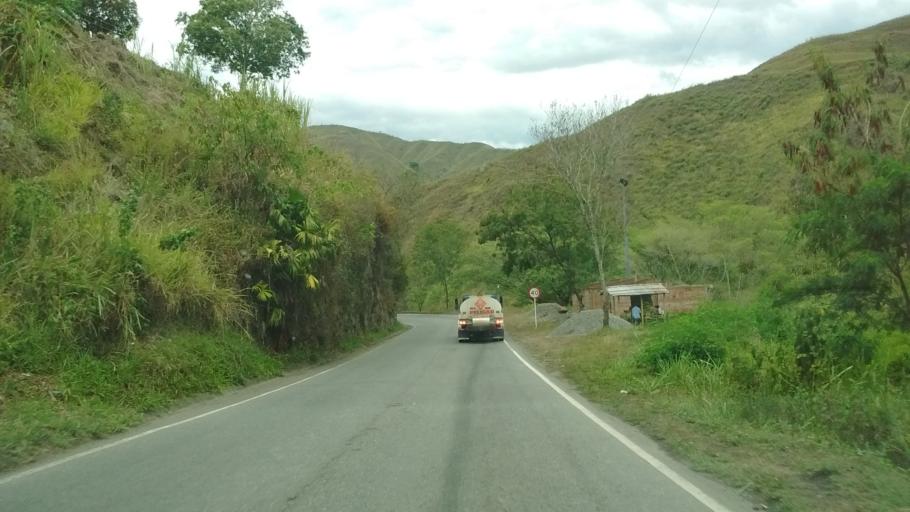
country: CO
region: Cauca
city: La Sierra
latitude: 2.1972
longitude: -76.8213
